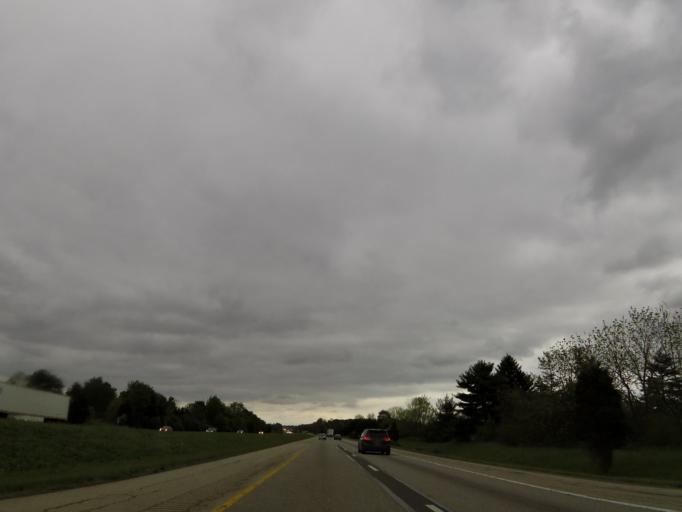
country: US
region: Ohio
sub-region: Warren County
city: Waynesville
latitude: 39.4383
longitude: -84.0592
